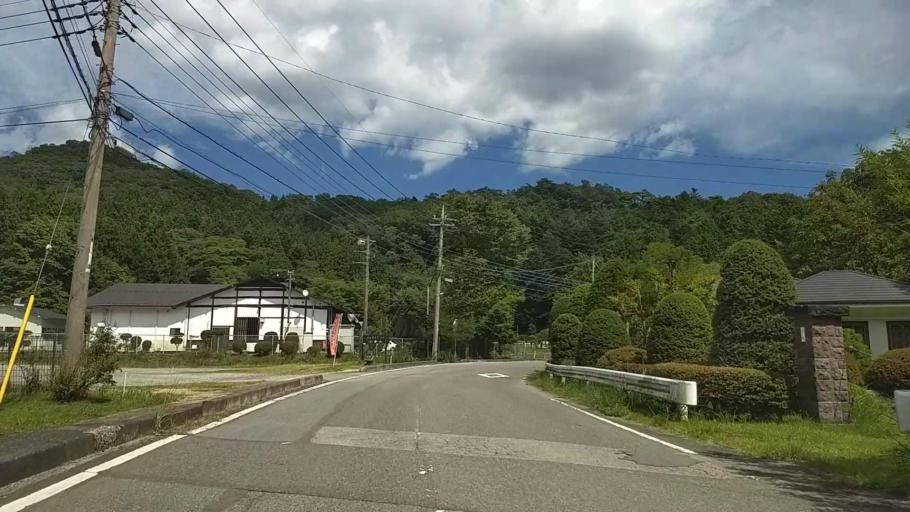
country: JP
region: Tochigi
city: Nikko
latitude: 36.7573
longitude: 139.6135
